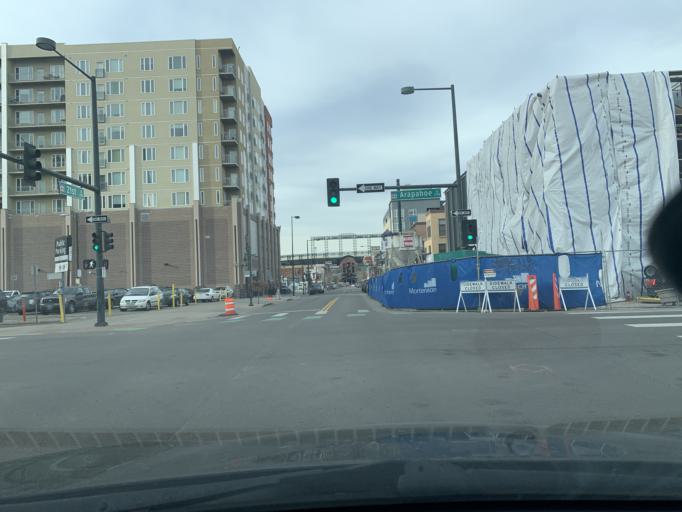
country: US
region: Colorado
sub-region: Denver County
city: Denver
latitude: 39.7525
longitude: -104.9896
